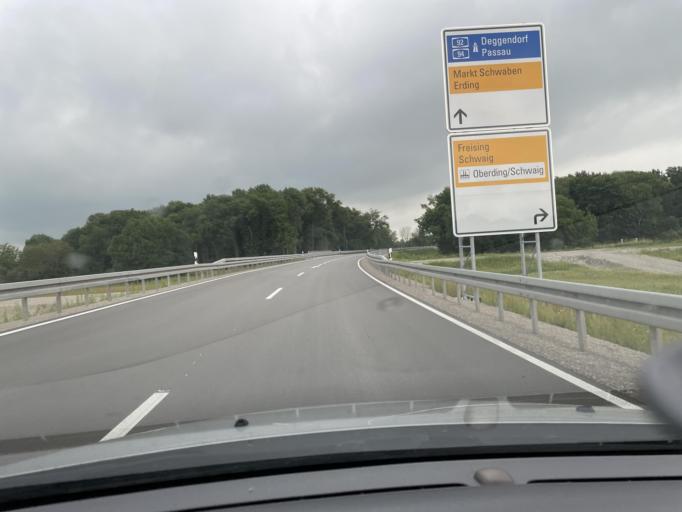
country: DE
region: Bavaria
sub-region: Upper Bavaria
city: Oberding
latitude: 48.3625
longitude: 11.8274
